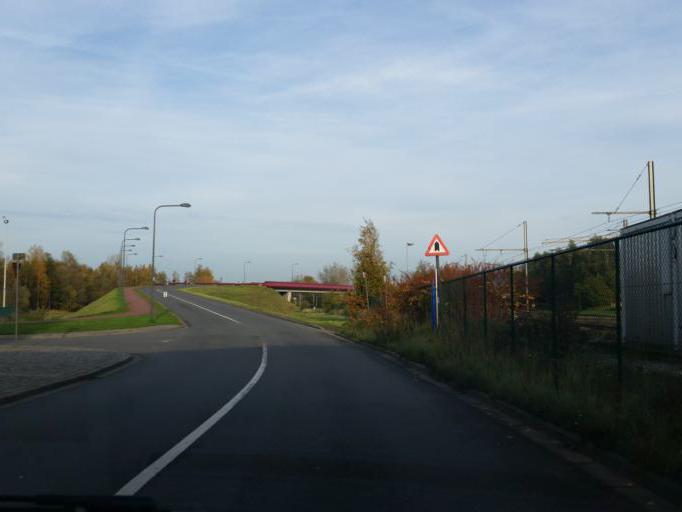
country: BE
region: Flanders
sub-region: Provincie Antwerpen
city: Hoboken
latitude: 51.1894
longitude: 4.3622
